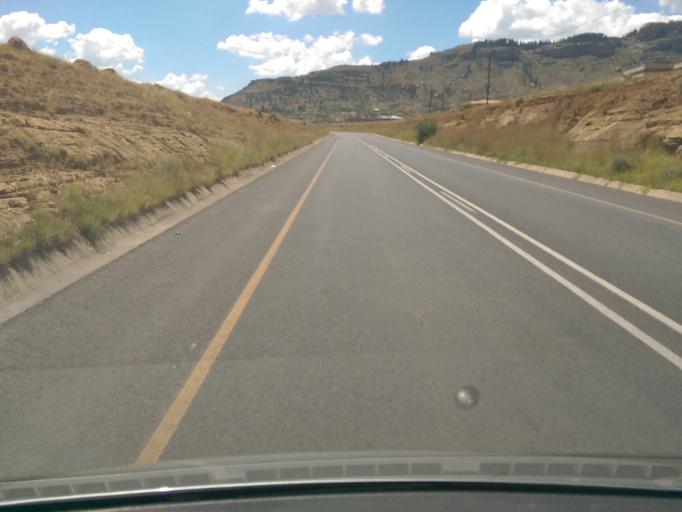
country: LS
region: Maseru
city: Maseru
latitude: -29.3713
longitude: 27.4747
